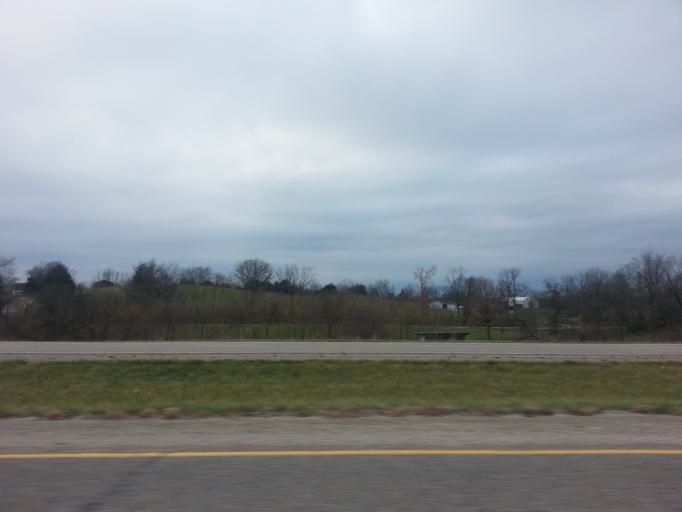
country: US
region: Iowa
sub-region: Henry County
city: Mount Pleasant
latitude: 40.9174
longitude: -91.5435
